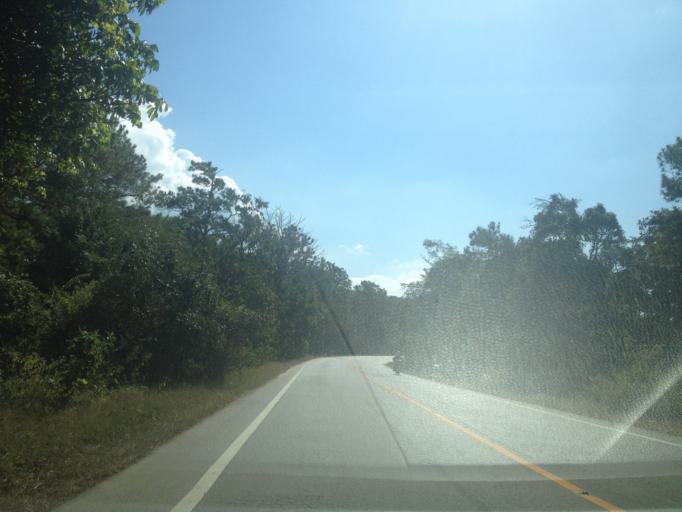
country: TH
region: Chiang Mai
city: Hot
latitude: 18.1503
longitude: 98.3845
